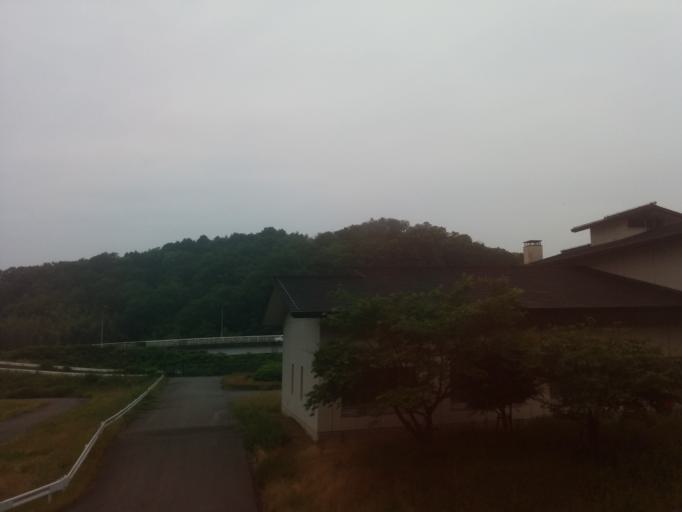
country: JP
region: Shiga Prefecture
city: Hikone
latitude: 35.2939
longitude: 136.2655
